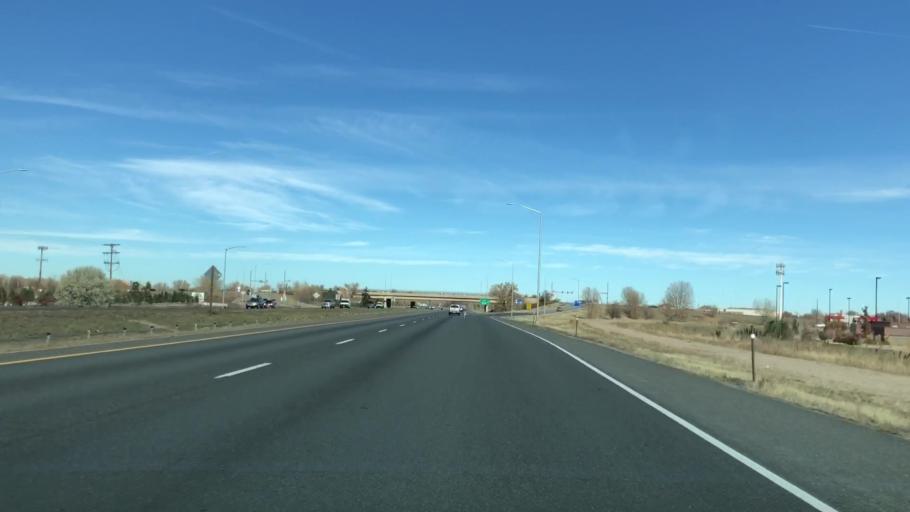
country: US
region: Colorado
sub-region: Weld County
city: Windsor
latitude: 40.5189
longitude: -104.9920
